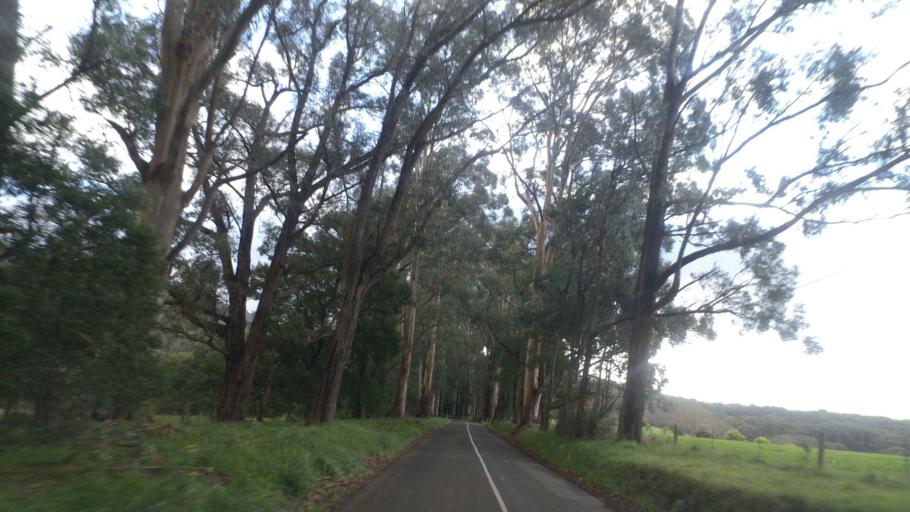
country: AU
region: Victoria
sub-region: Yarra Ranges
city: Monbulk
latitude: -37.9035
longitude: 145.4226
